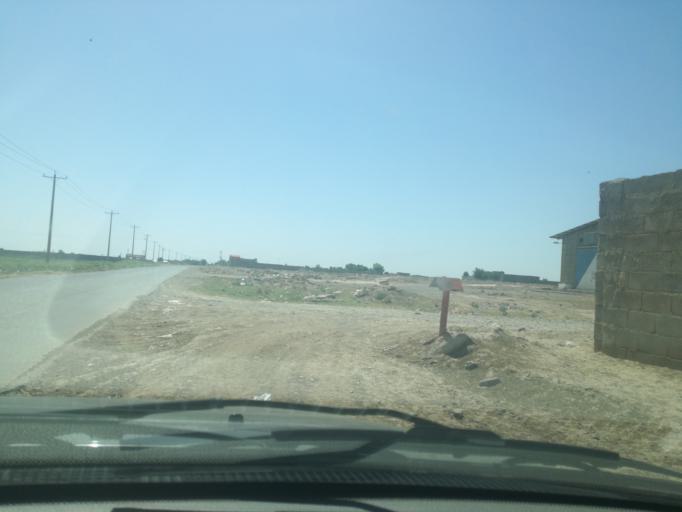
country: IR
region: Razavi Khorasan
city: Sarakhs
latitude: 36.5685
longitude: 61.1386
